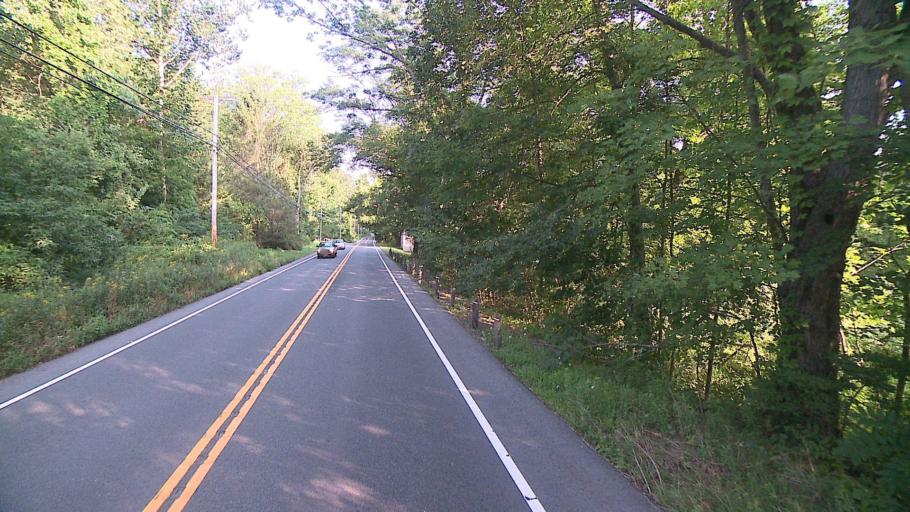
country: US
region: Connecticut
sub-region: Fairfield County
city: Sherman
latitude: 41.6289
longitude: -73.4684
